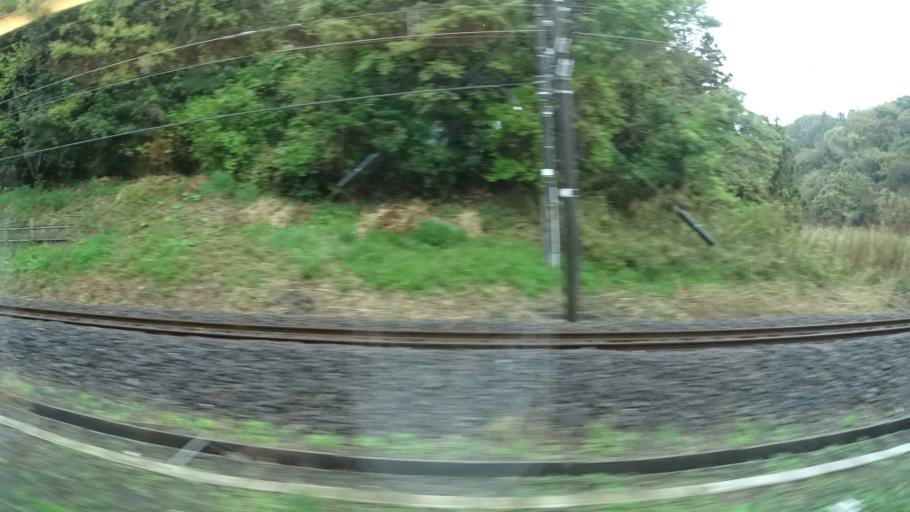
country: JP
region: Ibaraki
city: Kitaibaraki
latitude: 36.7604
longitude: 140.7358
